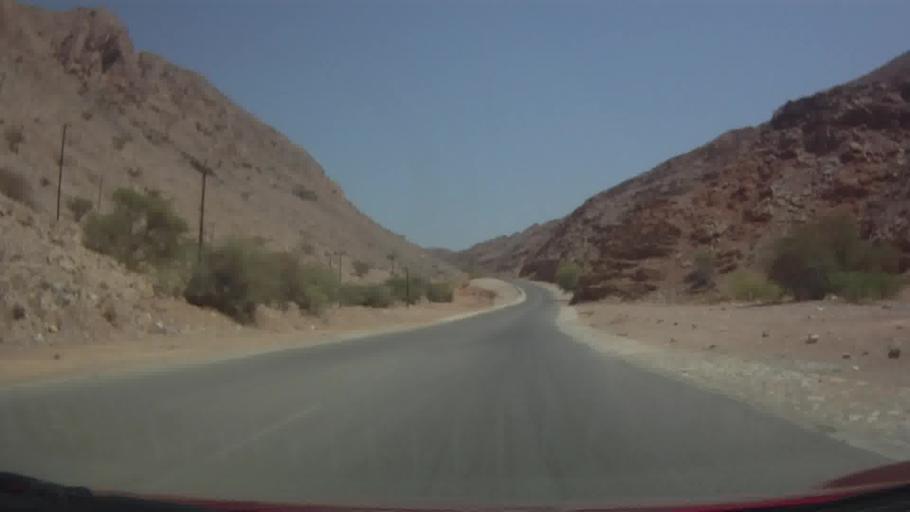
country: OM
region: Muhafazat Masqat
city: Muscat
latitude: 23.5093
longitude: 58.6692
